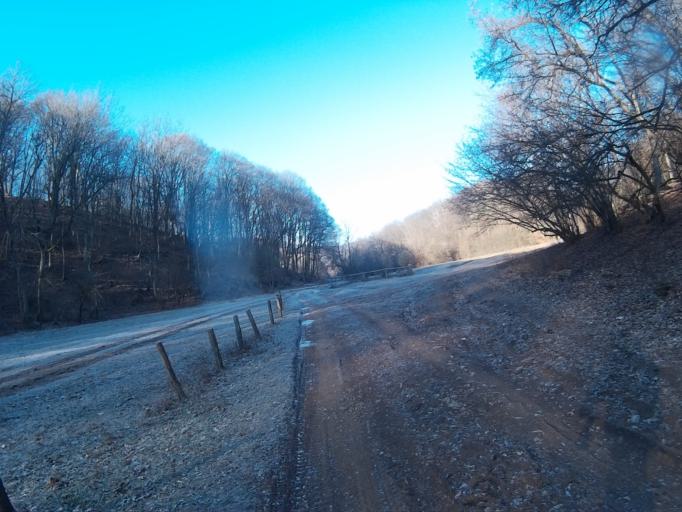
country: HU
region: Borsod-Abauj-Zemplen
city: Rudabanya
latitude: 48.4921
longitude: 20.5452
